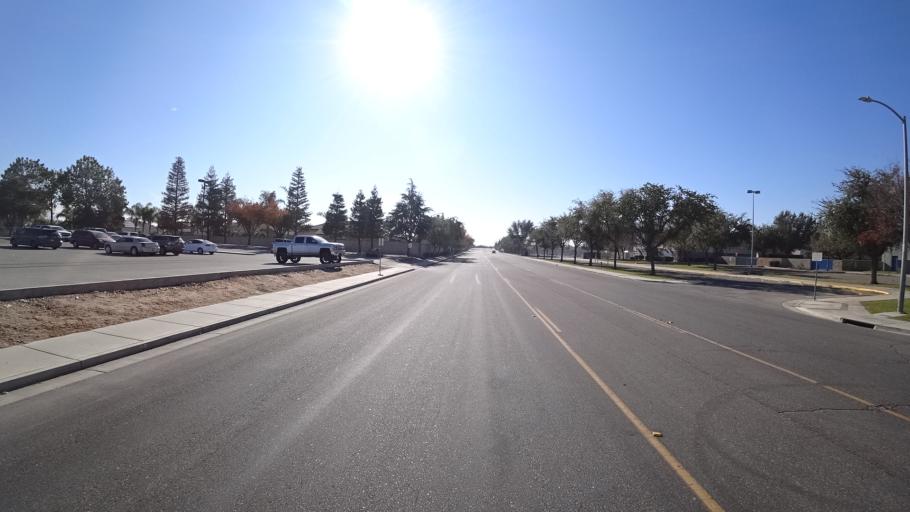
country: US
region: California
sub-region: Kern County
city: Rosedale
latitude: 35.3660
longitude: -119.1279
